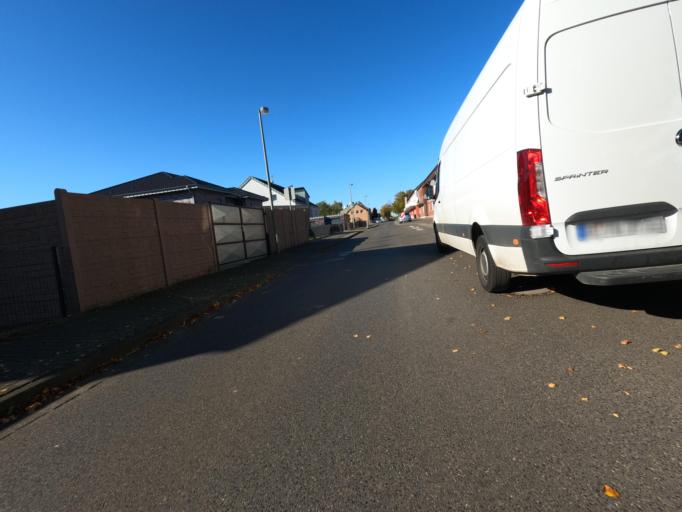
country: DE
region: North Rhine-Westphalia
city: Huckelhoven
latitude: 51.0496
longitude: 6.2453
